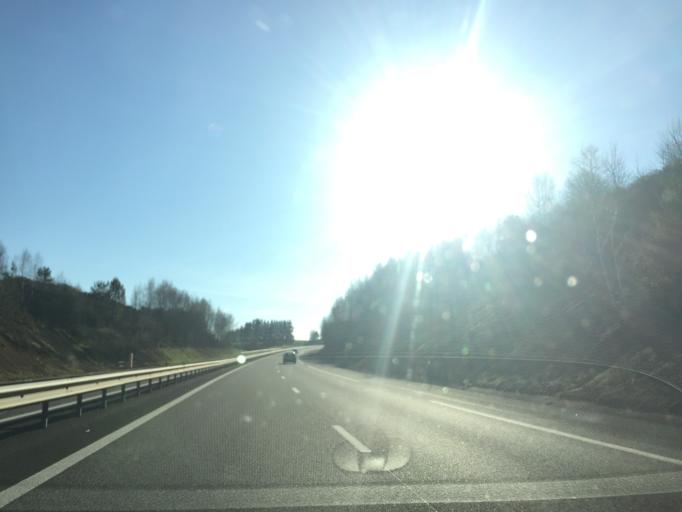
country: FR
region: Limousin
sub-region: Departement de la Correze
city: Sainte-Fereole
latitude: 45.2941
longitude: 1.5739
